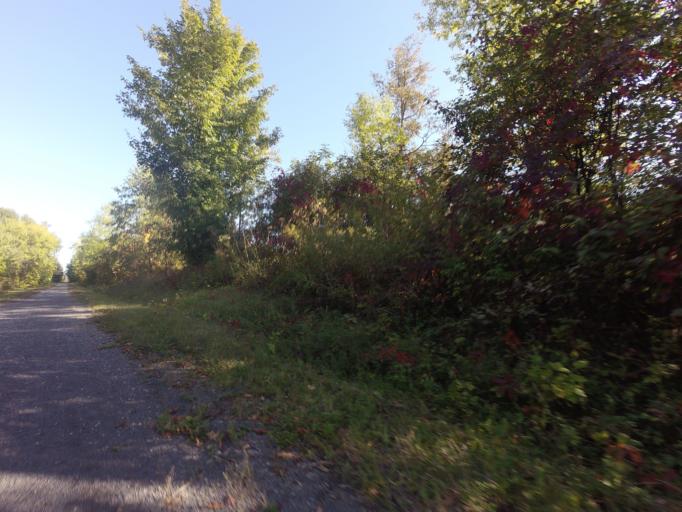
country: CA
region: Ontario
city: Hawkesbury
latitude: 45.5225
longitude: -74.5391
